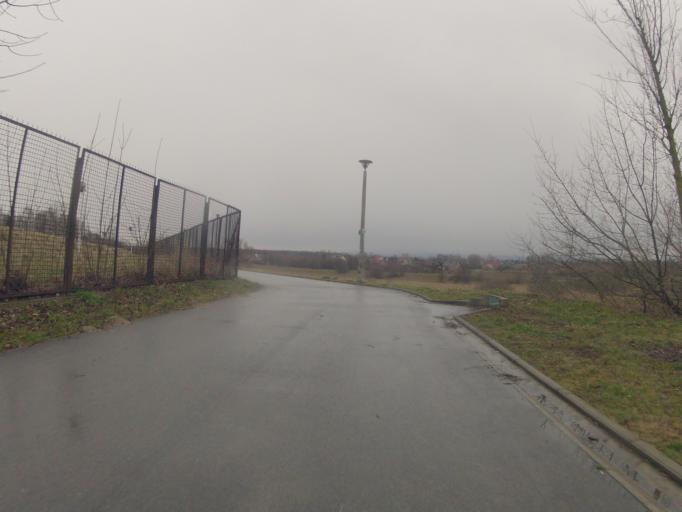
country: PL
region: Lesser Poland Voivodeship
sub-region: Powiat wielicki
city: Kokotow
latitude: 50.0649
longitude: 20.0435
